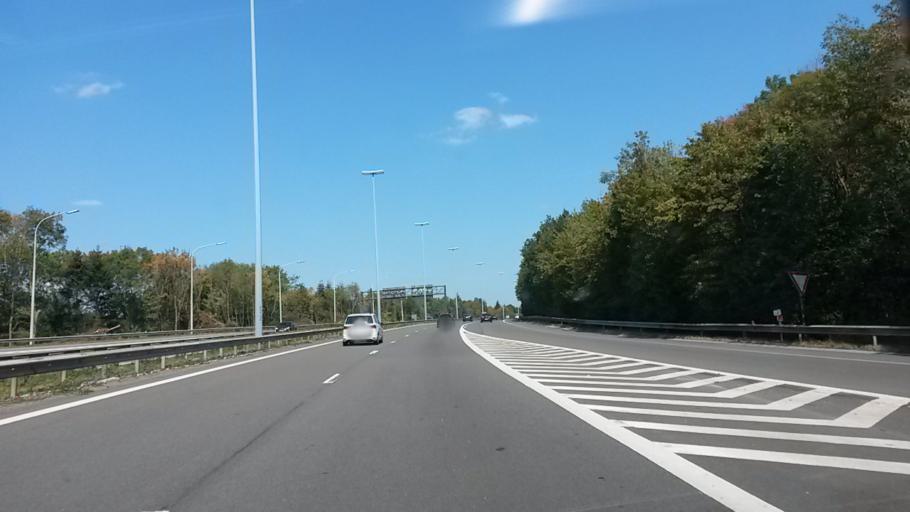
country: BE
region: Wallonia
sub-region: Province du Hainaut
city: Chatelet
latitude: 50.4233
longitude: 4.4963
